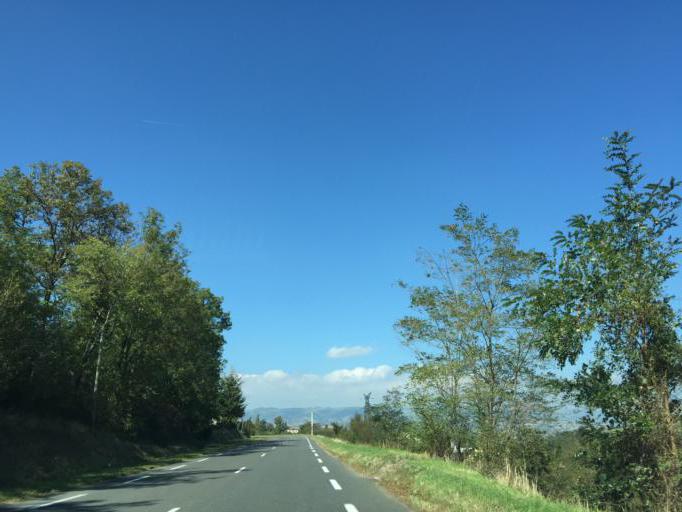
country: FR
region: Rhone-Alpes
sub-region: Departement de la Loire
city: Saint-Paul-en-Jarez
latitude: 45.4717
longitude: 4.5836
